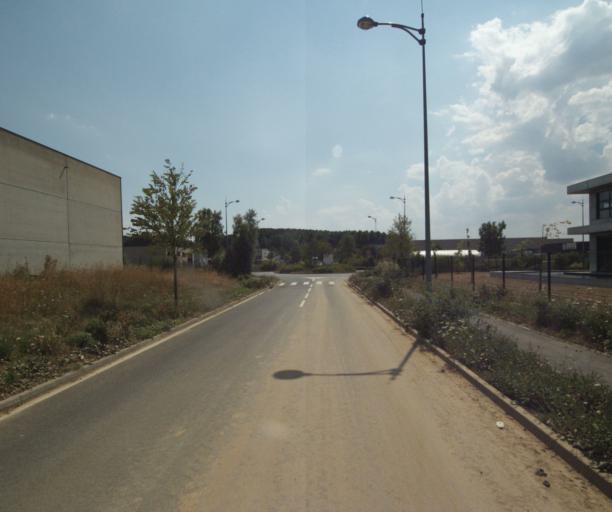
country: FR
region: Nord-Pas-de-Calais
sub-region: Departement du Nord
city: Comines
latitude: 50.7536
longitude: 2.9946
